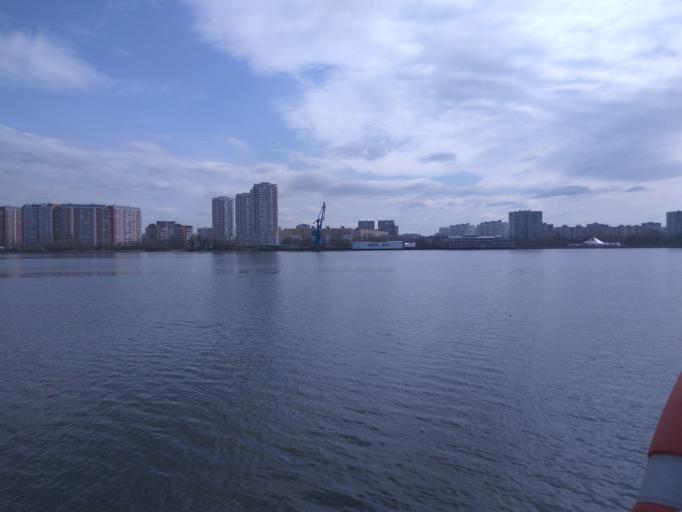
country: RU
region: Moscow
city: Kolomenskoye
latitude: 55.6881
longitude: 37.7071
